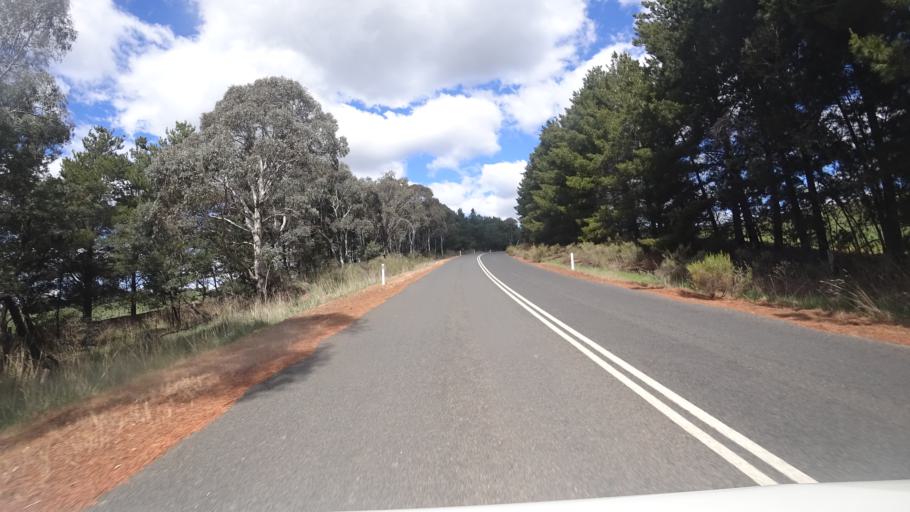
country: AU
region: New South Wales
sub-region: Oberon
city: Oberon
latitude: -33.6693
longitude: 149.7812
